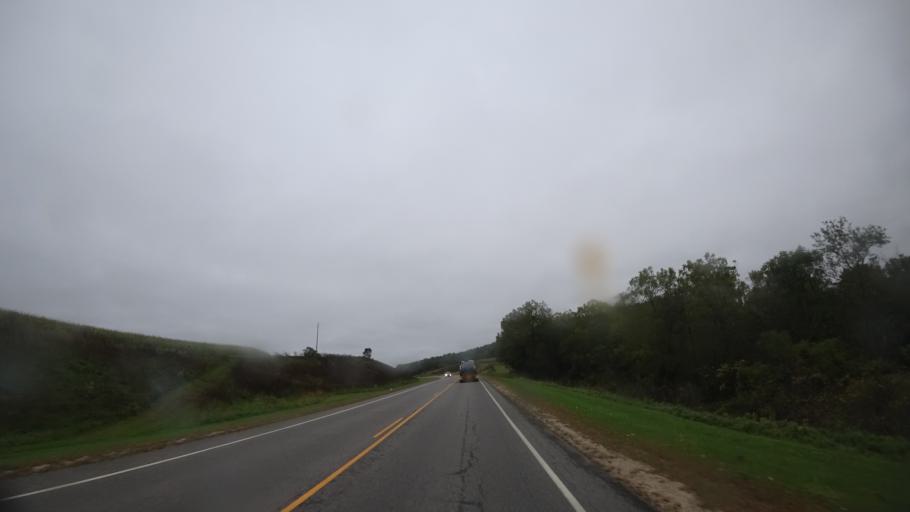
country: US
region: Wisconsin
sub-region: Crawford County
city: Prairie du Chien
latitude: 43.0305
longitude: -91.0097
